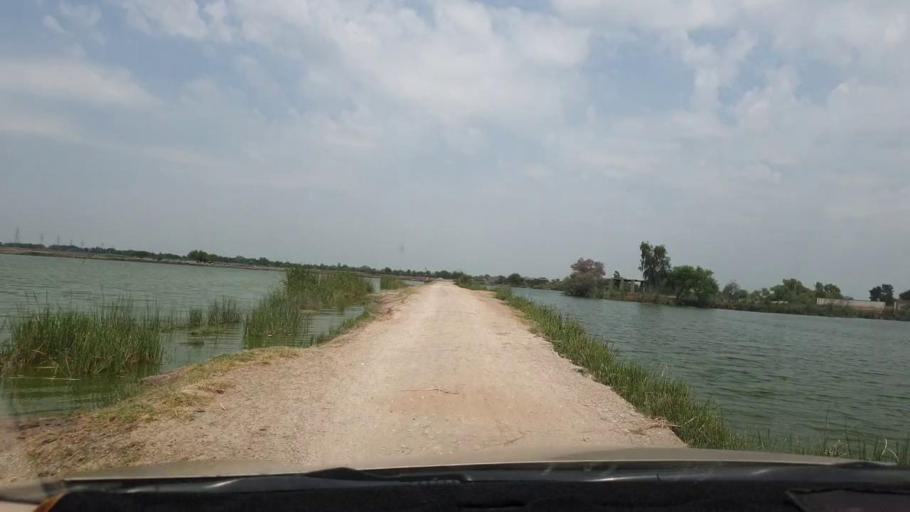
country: PK
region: Sindh
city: Naudero
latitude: 27.7254
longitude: 68.3401
